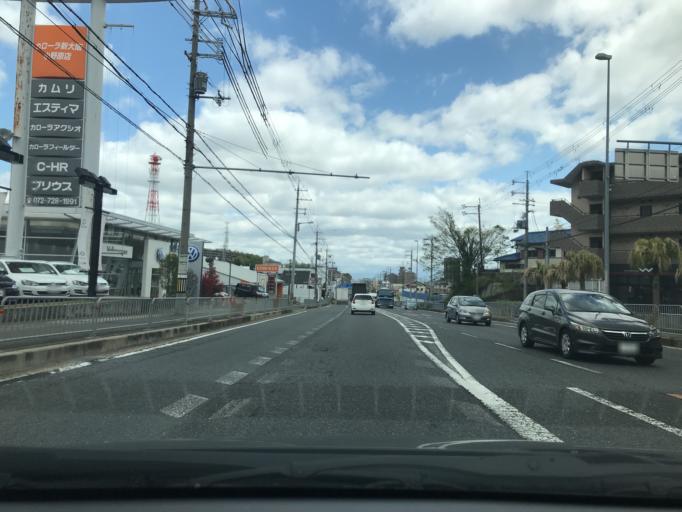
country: JP
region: Osaka
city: Mino
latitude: 34.8357
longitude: 135.5092
